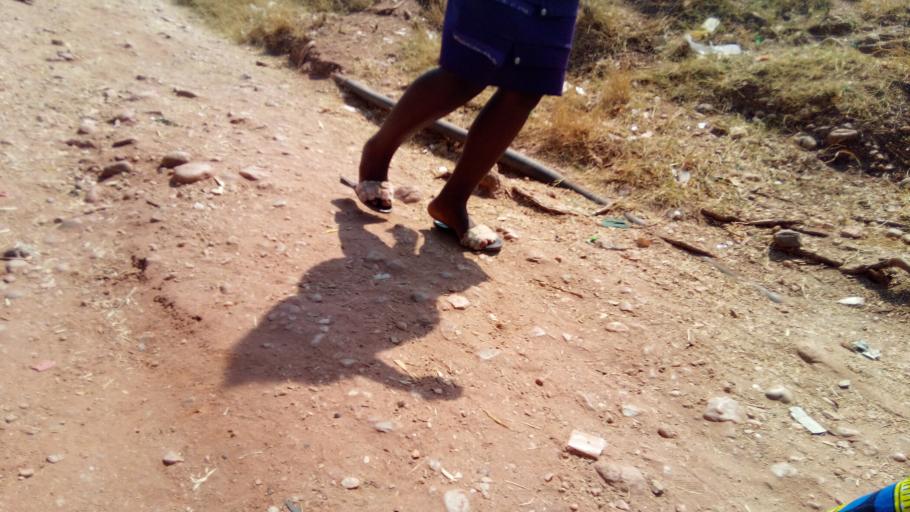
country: CD
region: Katanga
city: Kalemie
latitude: -5.9319
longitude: 29.1887
